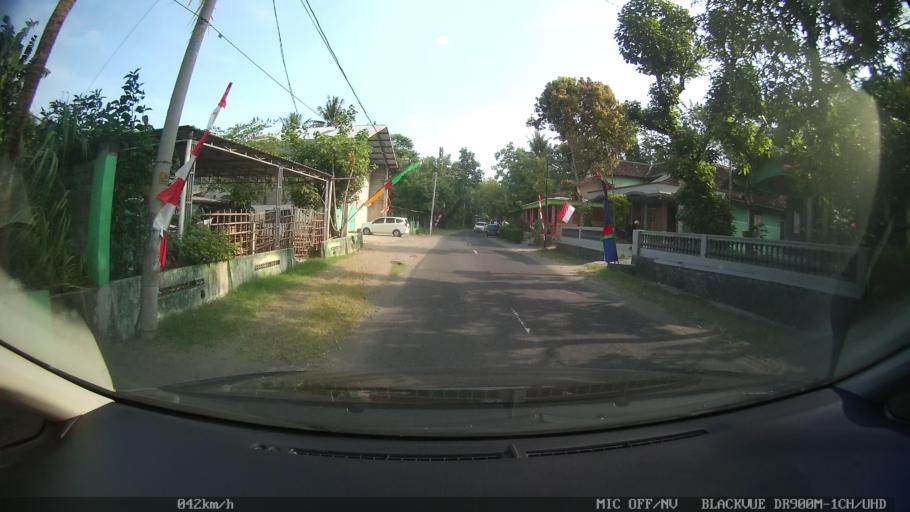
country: ID
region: Daerah Istimewa Yogyakarta
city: Bantul
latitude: -7.8696
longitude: 110.3178
